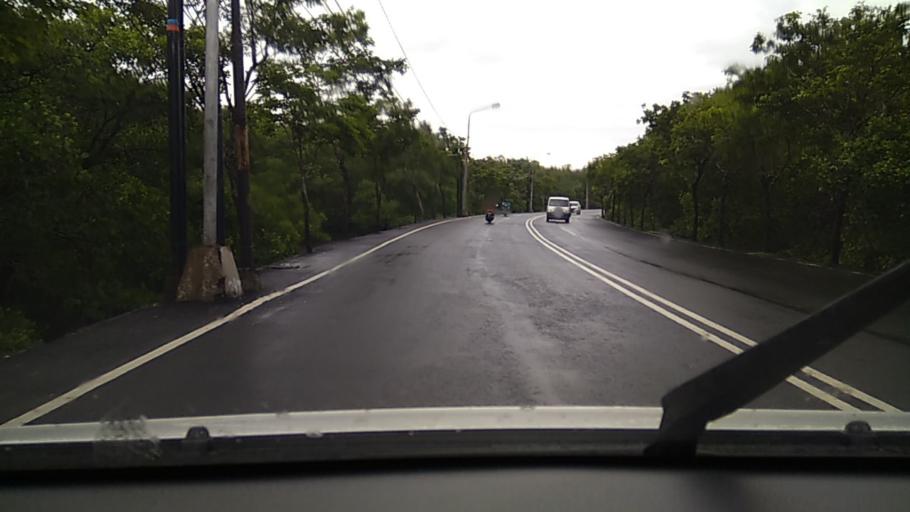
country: ID
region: Bali
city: Bualu
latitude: -8.7916
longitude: 115.2171
